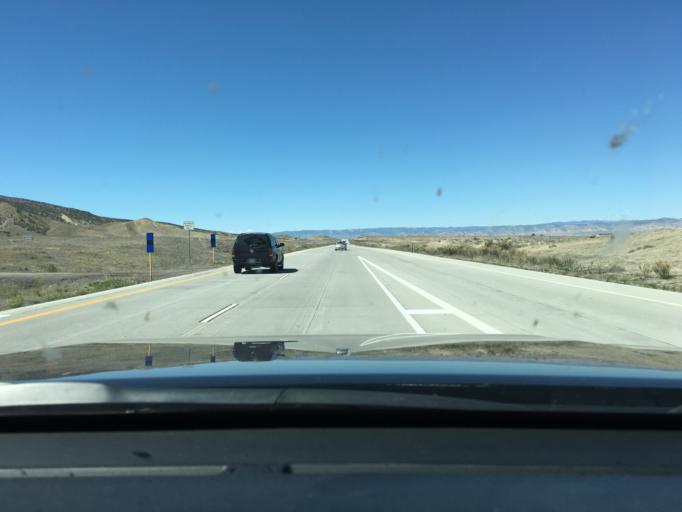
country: US
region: Colorado
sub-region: Mesa County
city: Loma
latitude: 39.1840
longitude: -108.8297
